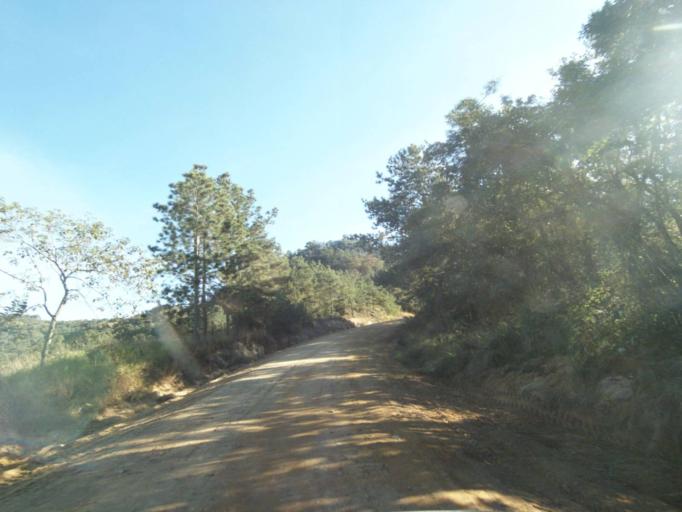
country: BR
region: Parana
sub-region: Tibagi
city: Tibagi
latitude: -24.5389
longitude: -50.5290
